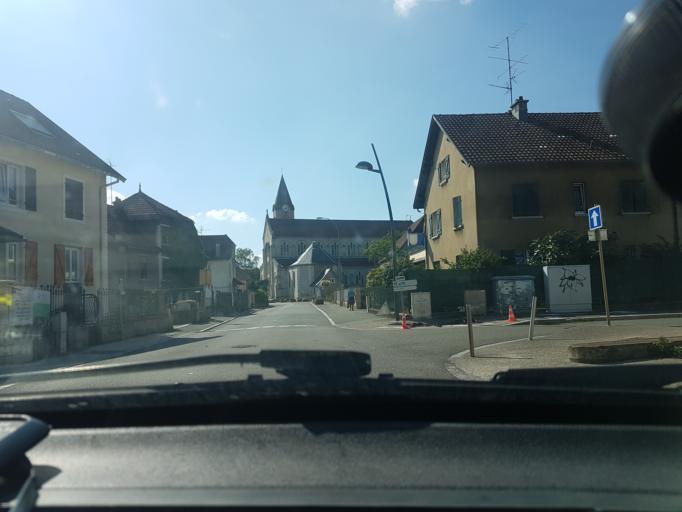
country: FR
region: Franche-Comte
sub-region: Territoire de Belfort
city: Danjoutin
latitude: 47.6181
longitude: 6.8642
